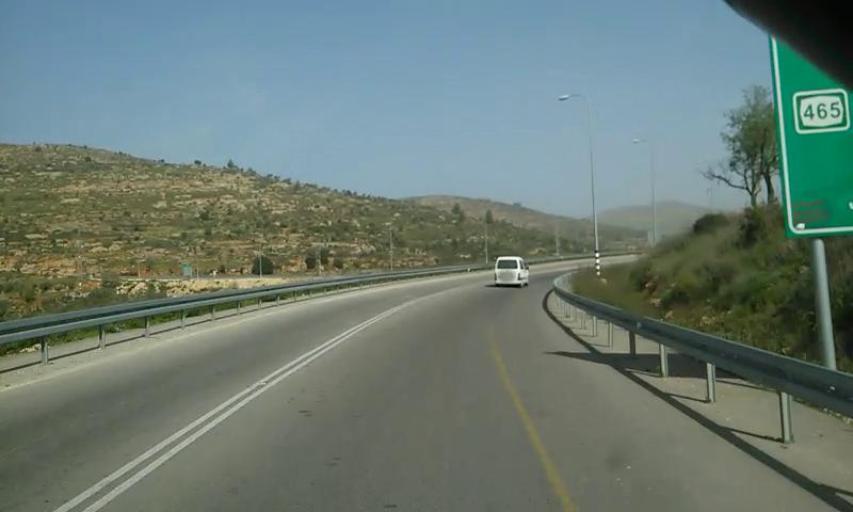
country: PS
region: West Bank
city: `Atarah
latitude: 31.9880
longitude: 35.2273
